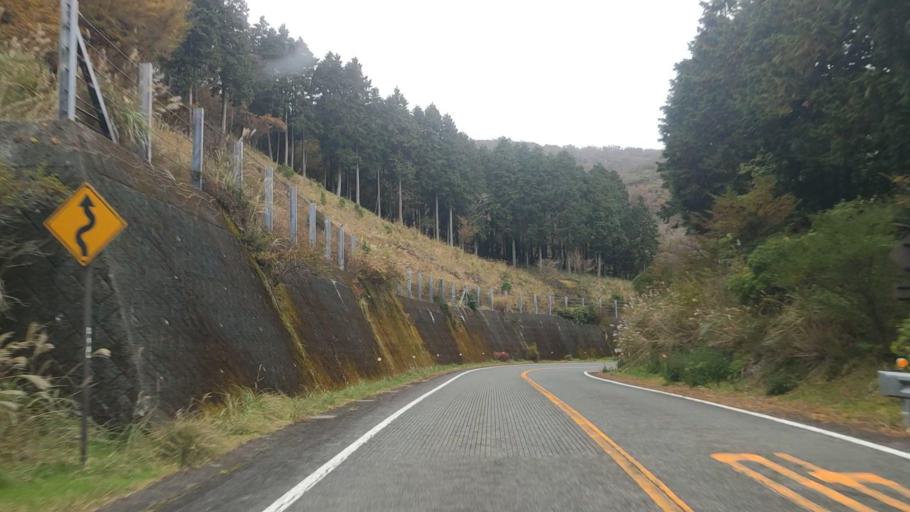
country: JP
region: Shizuoka
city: Heda
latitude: 34.8782
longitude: 138.8381
